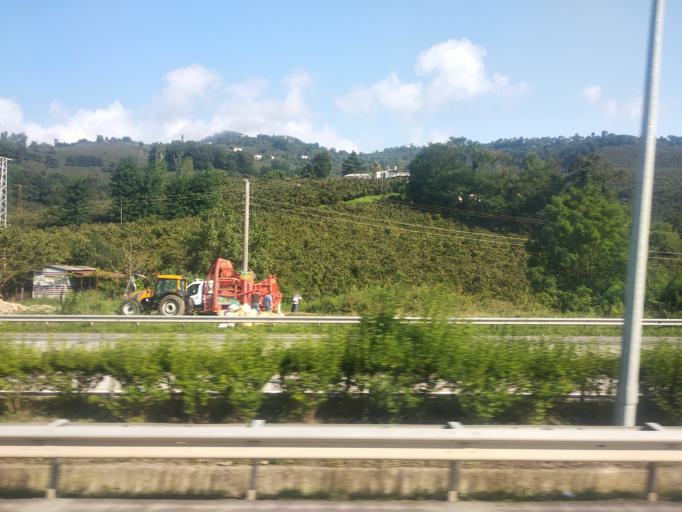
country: TR
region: Ordu
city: Ordu
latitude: 41.0085
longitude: 37.8303
